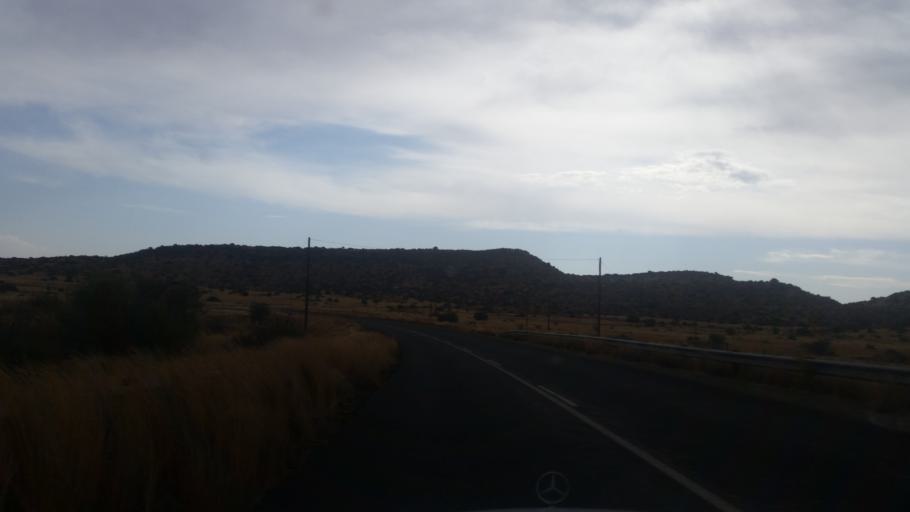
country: ZA
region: Orange Free State
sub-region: Xhariep District Municipality
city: Trompsburg
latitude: -30.4263
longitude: 26.1082
